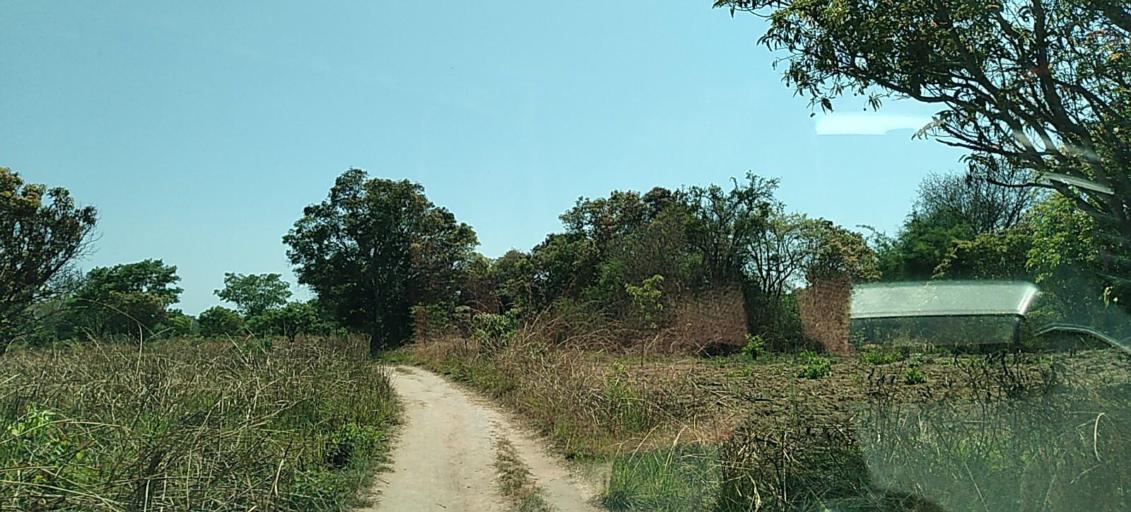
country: ZM
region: Copperbelt
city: Chililabombwe
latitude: -12.2861
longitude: 27.8812
